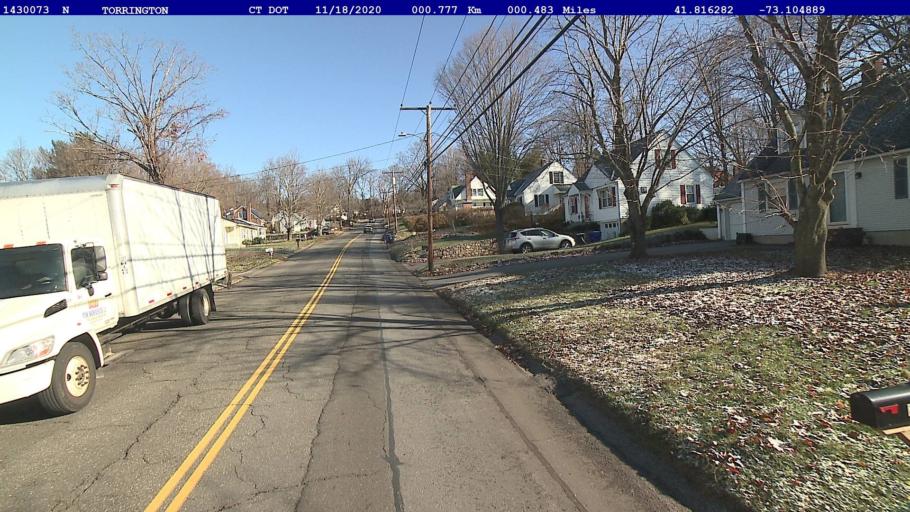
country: US
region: Connecticut
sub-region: Litchfield County
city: Torrington
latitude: 41.8163
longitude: -73.1049
